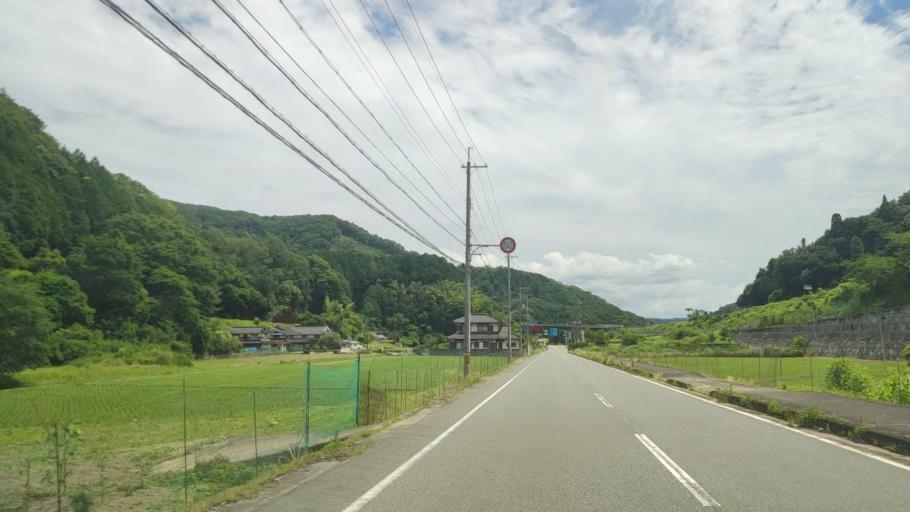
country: JP
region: Hyogo
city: Yamazakicho-nakabirose
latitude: 35.0614
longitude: 134.3648
